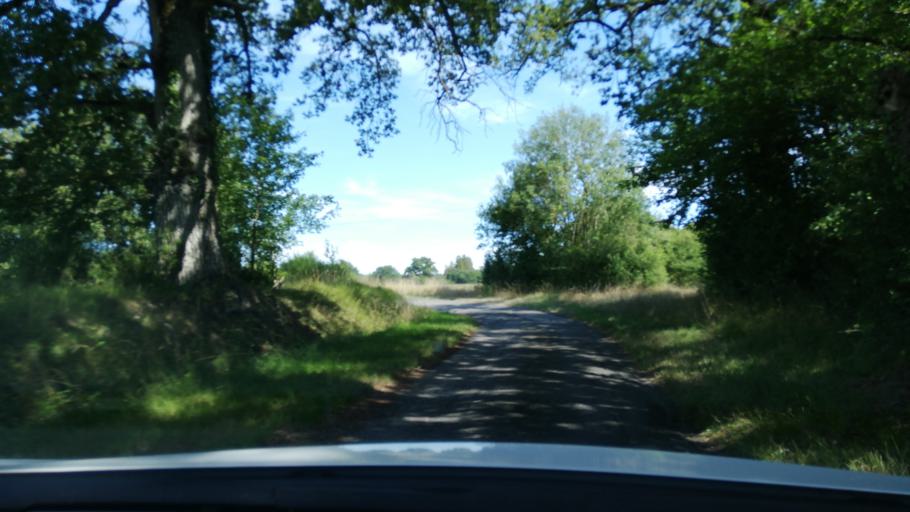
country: FR
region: Centre
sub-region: Departement d'Indre-et-Loire
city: Mazieres-de-Touraine
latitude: 47.3951
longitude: 0.4443
